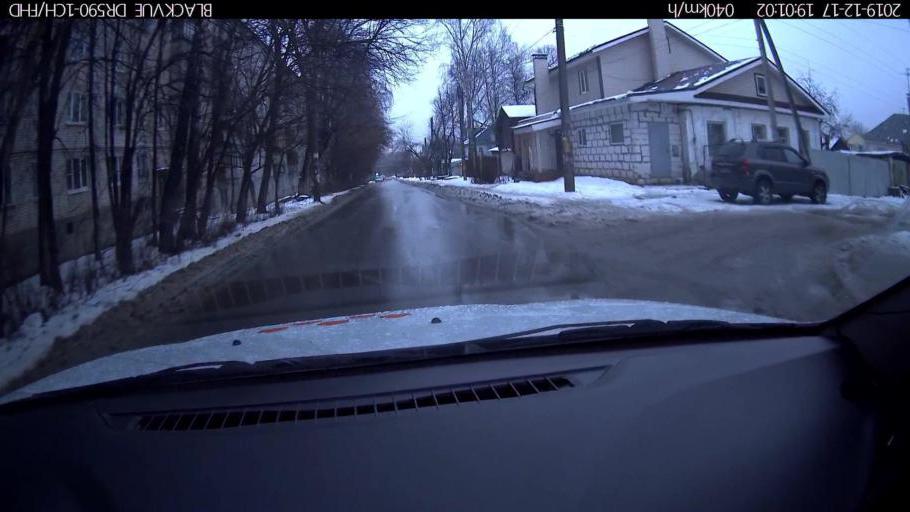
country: RU
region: Nizjnij Novgorod
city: Nizhniy Novgorod
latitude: 56.2927
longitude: 44.0283
